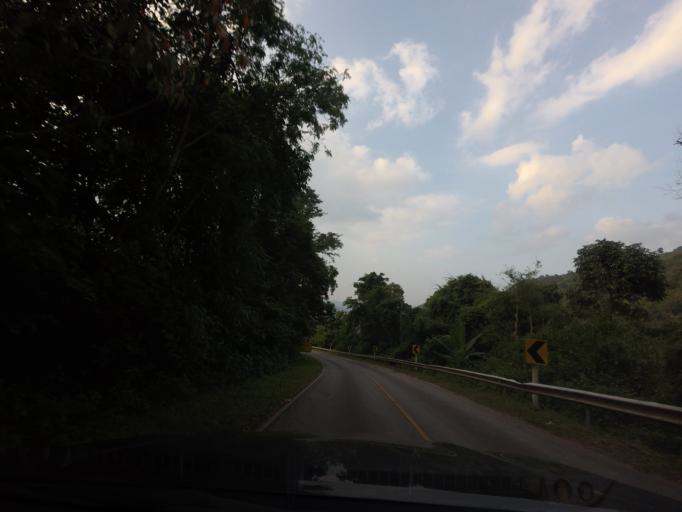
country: TH
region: Loei
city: Na Haeo
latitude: 17.3671
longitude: 101.0500
